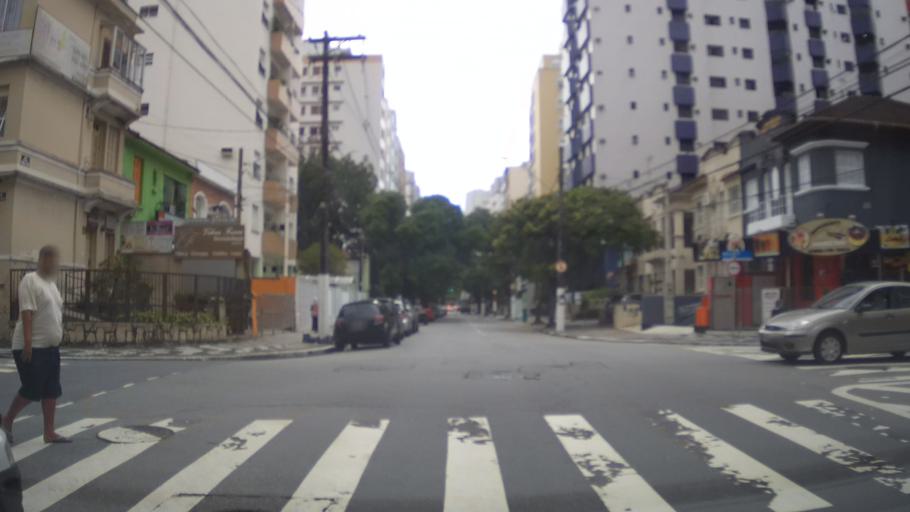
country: BR
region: Sao Paulo
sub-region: Santos
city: Santos
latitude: -23.9690
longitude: -46.3271
